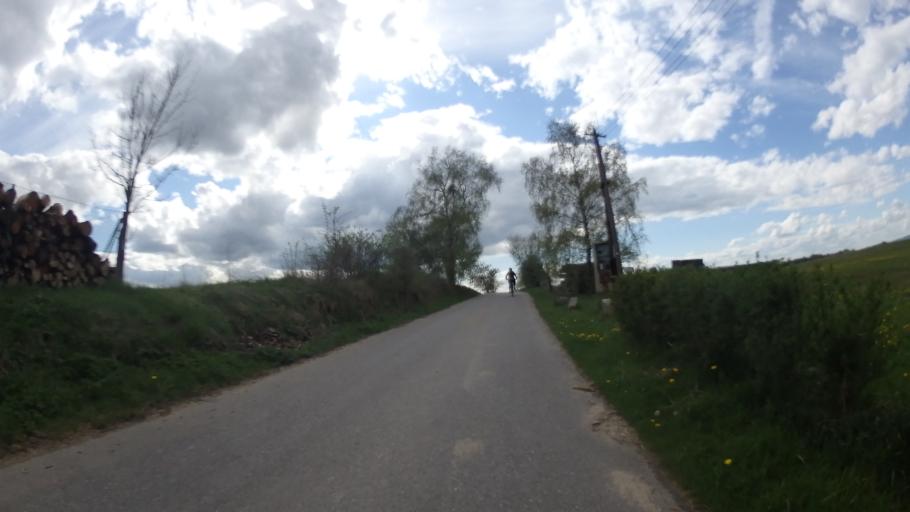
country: CZ
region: Vysocina
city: Merin
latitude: 49.3578
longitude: 15.9336
